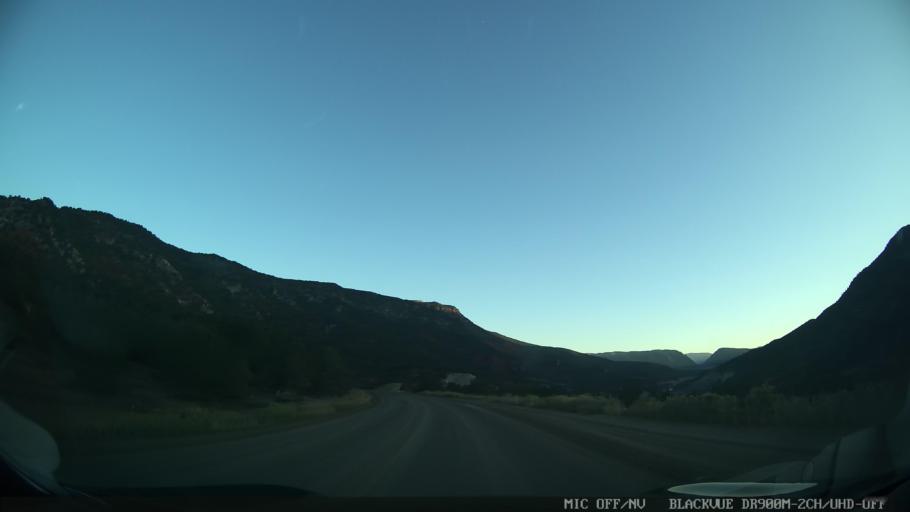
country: US
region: Colorado
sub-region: Eagle County
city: Edwards
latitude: 39.8634
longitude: -106.6435
